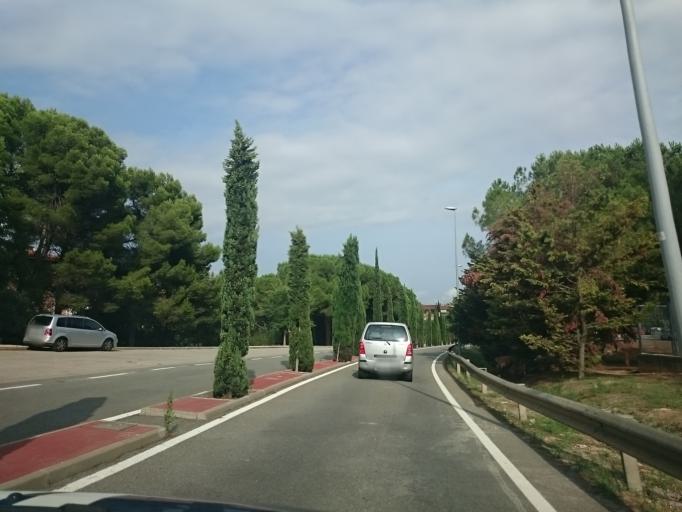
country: ES
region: Catalonia
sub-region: Provincia de Barcelona
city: Sant Cugat del Valles
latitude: 41.4828
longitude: 2.0862
